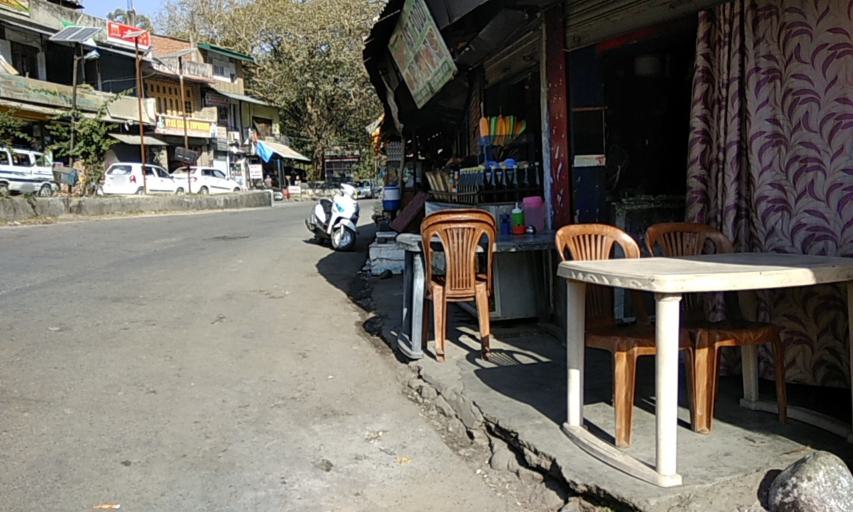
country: IN
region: Himachal Pradesh
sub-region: Kangra
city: Palampur
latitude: 32.0831
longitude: 76.5154
